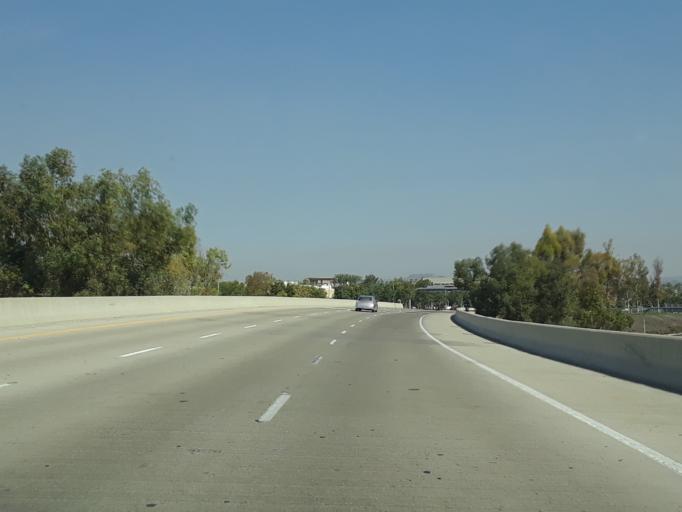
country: US
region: California
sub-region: Orange County
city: Tustin
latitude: 33.7146
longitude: -117.7986
